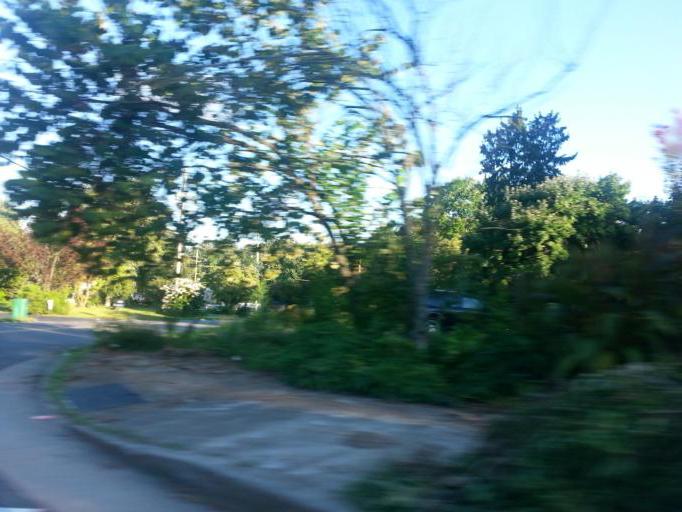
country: US
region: Tennessee
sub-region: Knox County
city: Knoxville
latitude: 35.9416
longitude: -84.0342
